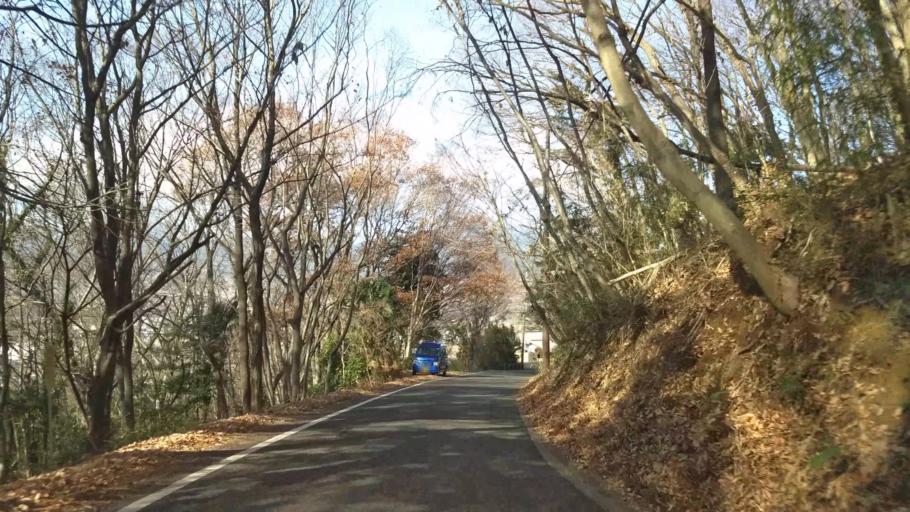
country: JP
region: Kanagawa
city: Hadano
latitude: 35.3763
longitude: 139.2449
